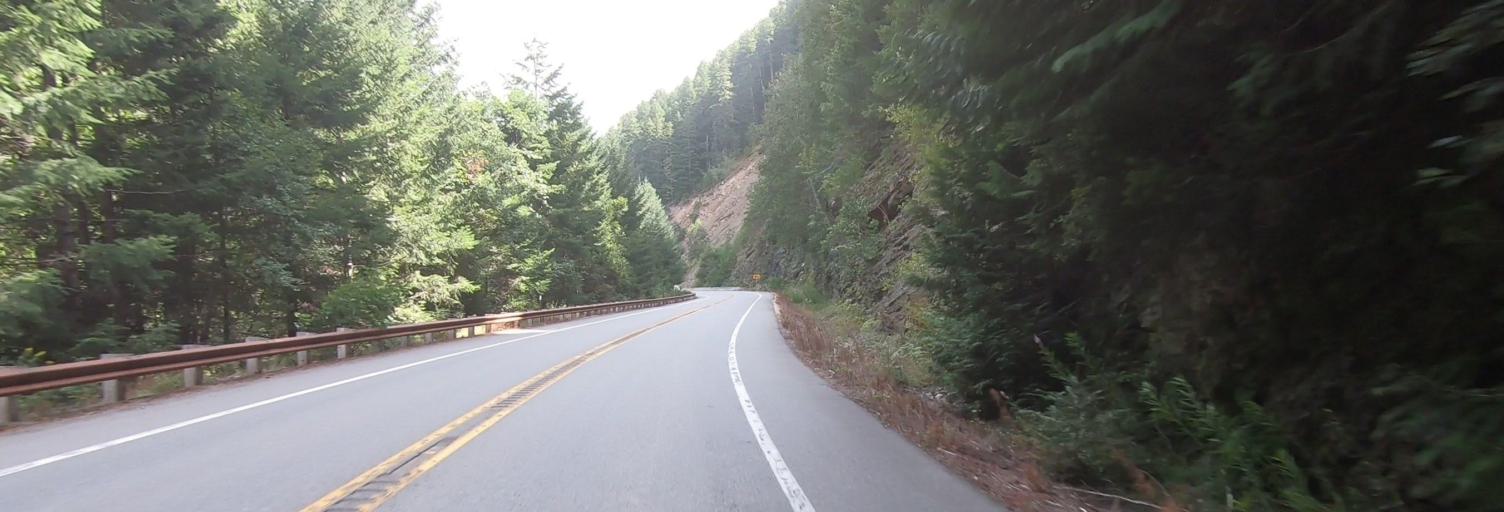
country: US
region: Washington
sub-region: Snohomish County
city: Darrington
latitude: 48.6992
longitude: -120.9107
